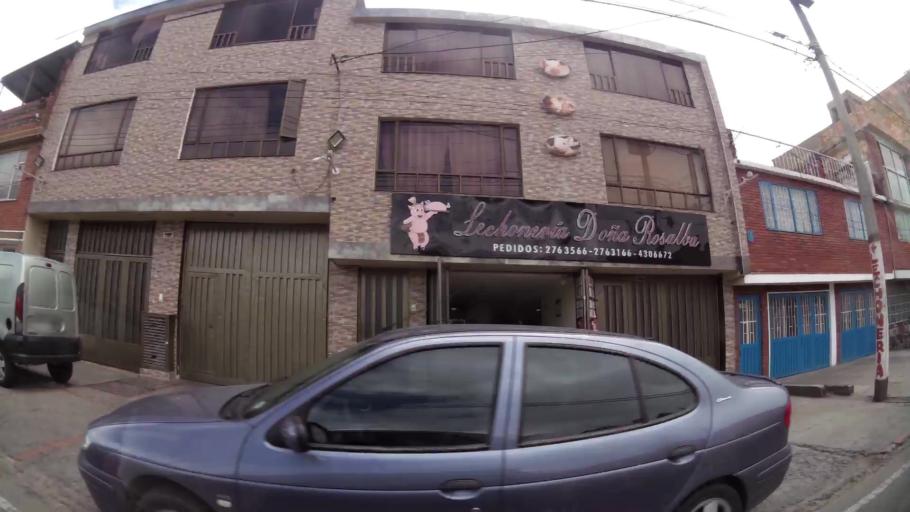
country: CO
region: Bogota D.C.
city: Barrio San Luis
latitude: 4.6971
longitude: -74.1012
